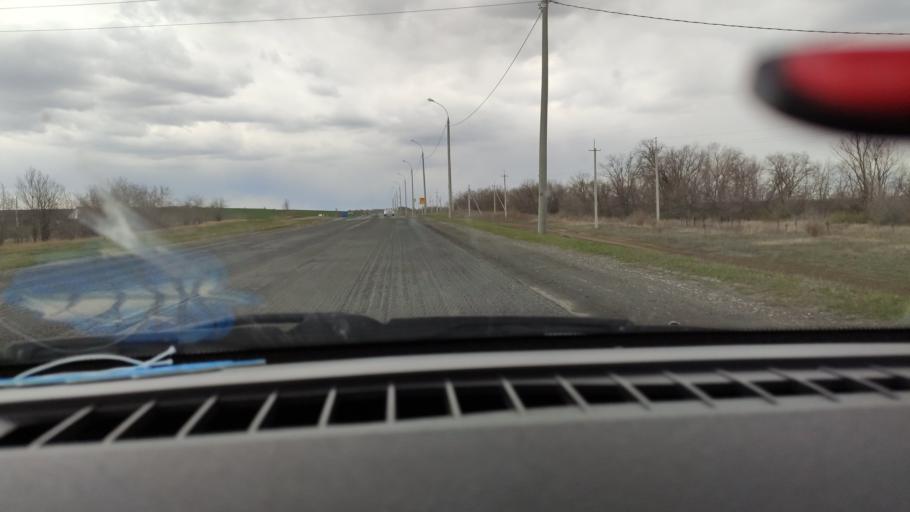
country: RU
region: Saratov
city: Shumeyka
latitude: 51.7909
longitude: 46.1531
